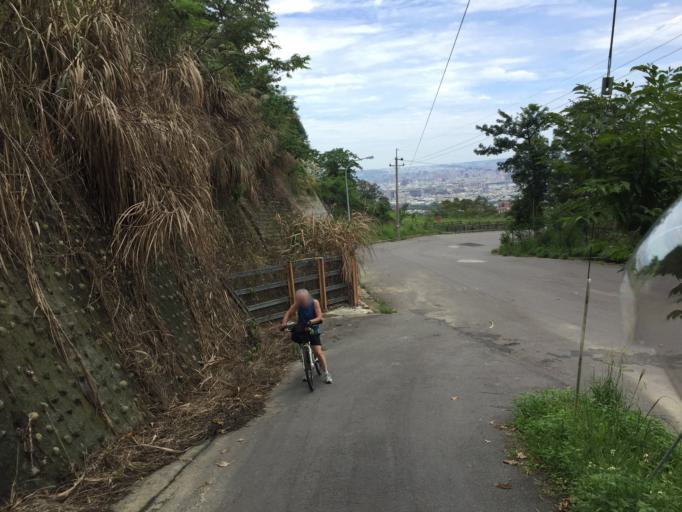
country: TW
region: Taiwan
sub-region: Taichung City
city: Taichung
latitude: 24.0642
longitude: 120.7189
